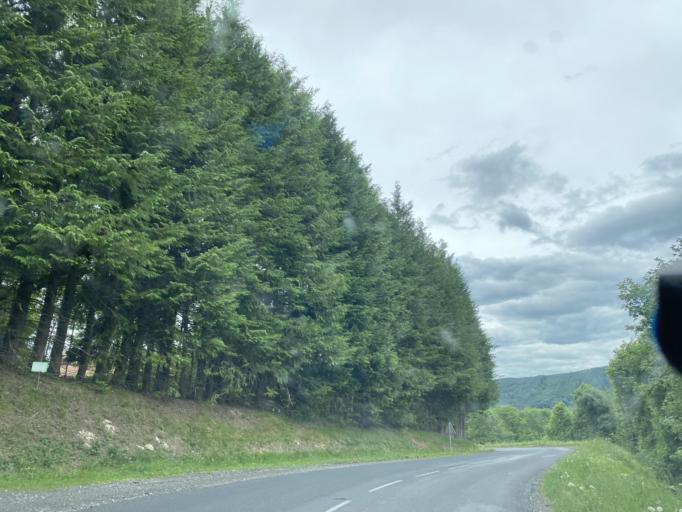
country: FR
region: Rhone-Alpes
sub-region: Departement de la Loire
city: Noiretable
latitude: 45.7846
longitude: 3.6848
